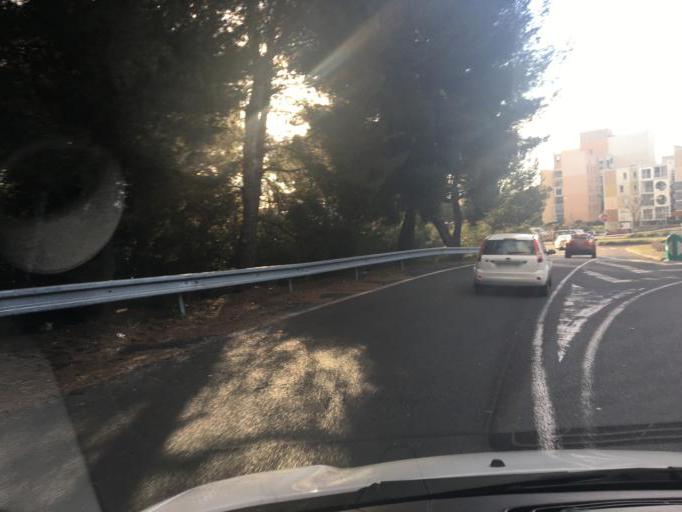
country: FR
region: Provence-Alpes-Cote d'Azur
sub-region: Departement des Bouches-du-Rhone
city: Martigues
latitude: 43.4109
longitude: 5.0405
